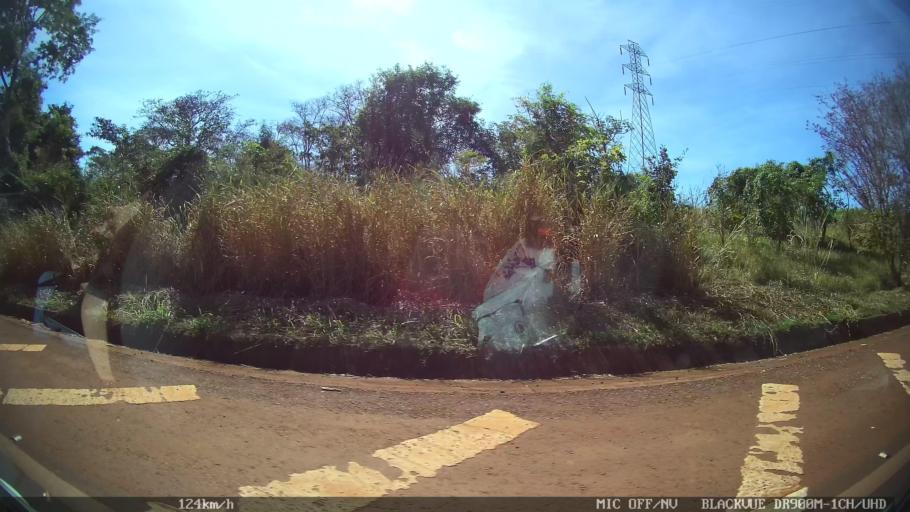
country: BR
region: Sao Paulo
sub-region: Sao Joaquim Da Barra
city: Sao Joaquim da Barra
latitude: -20.5394
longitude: -47.8170
